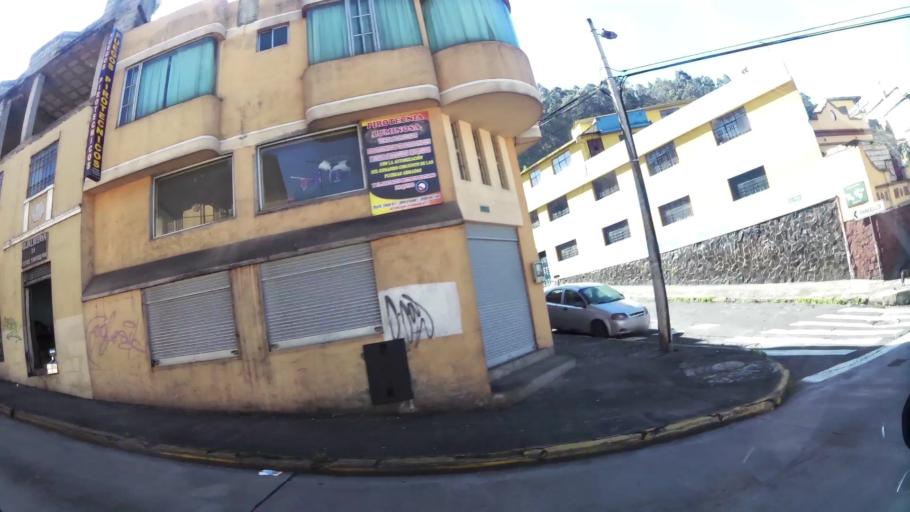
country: EC
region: Pichincha
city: Quito
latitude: -0.2295
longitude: -78.5229
